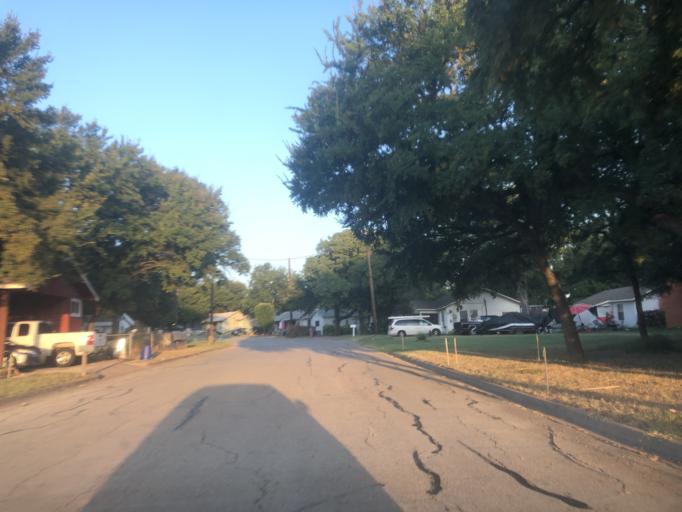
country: US
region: Texas
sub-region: Tarrant County
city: Lake Worth
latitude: 32.8078
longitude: -97.4469
